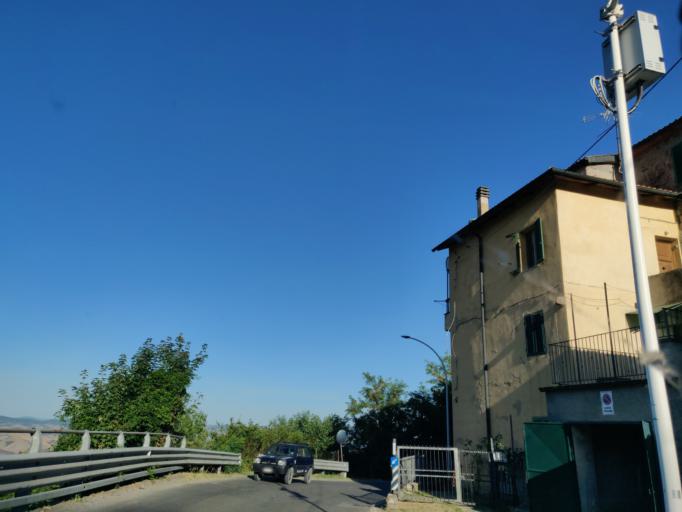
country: IT
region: Tuscany
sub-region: Provincia di Siena
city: Piancastagnaio
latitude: 42.8497
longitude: 11.6947
